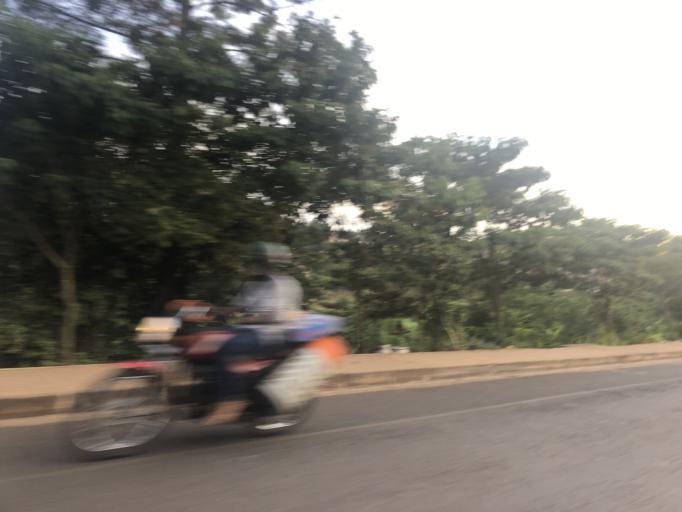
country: RW
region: Kigali
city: Kigali
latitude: -1.9318
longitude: 30.0879
